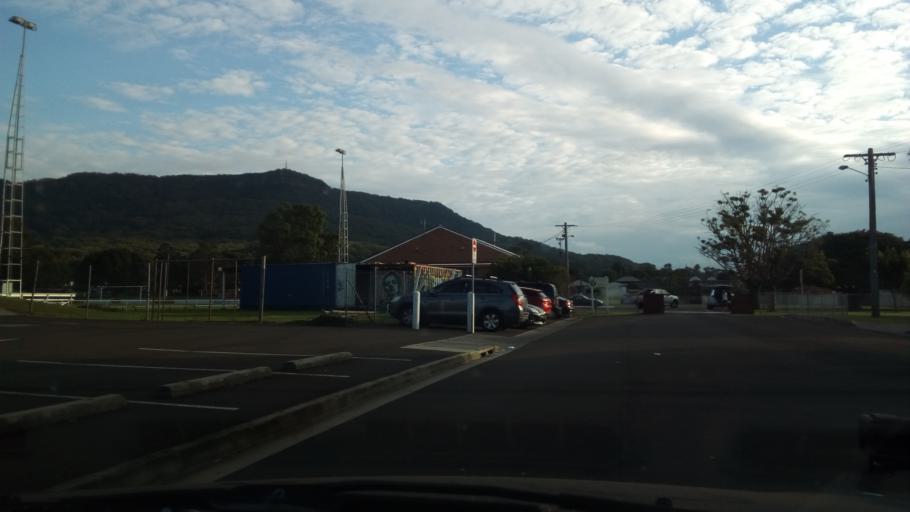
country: AU
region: New South Wales
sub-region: Wollongong
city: Fairy Meadow
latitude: -34.3867
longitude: 150.8840
